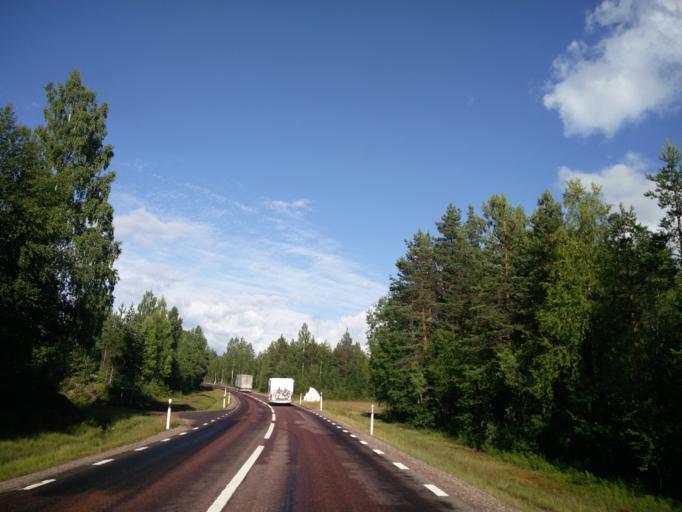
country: SE
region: Vaermland
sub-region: Hagfors Kommun
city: Ekshaerad
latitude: 60.4828
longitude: 13.4003
